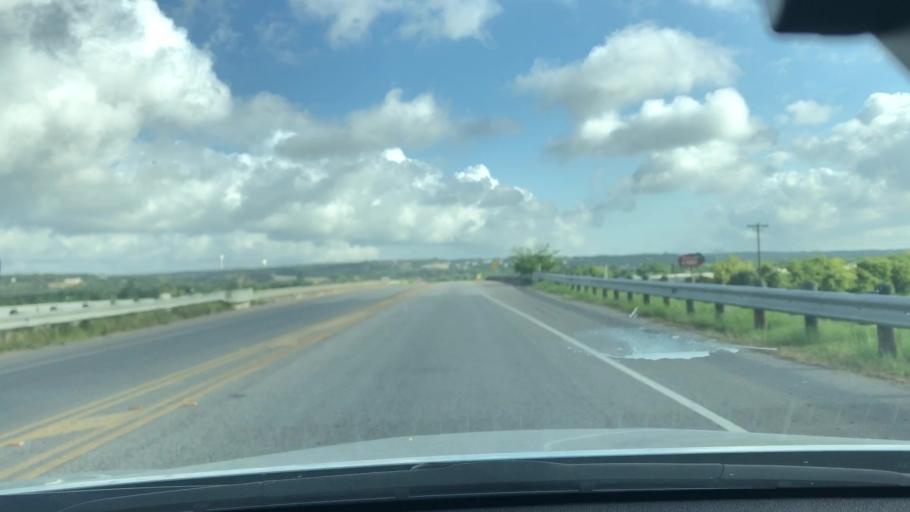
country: US
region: Texas
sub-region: Comal County
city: New Braunfels
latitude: 29.6820
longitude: -98.1543
